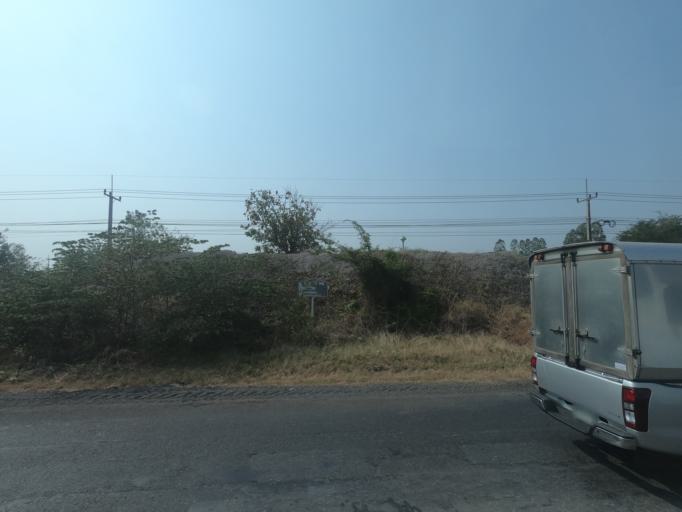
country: TH
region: Nakhon Ratchasima
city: Sida
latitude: 15.6042
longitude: 102.5618
